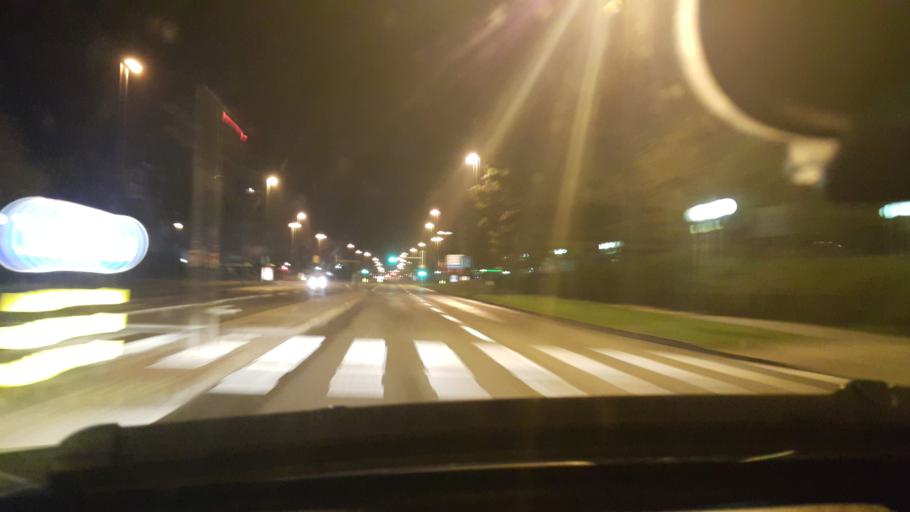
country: SI
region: Maribor
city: Maribor
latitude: 46.5435
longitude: 15.6316
